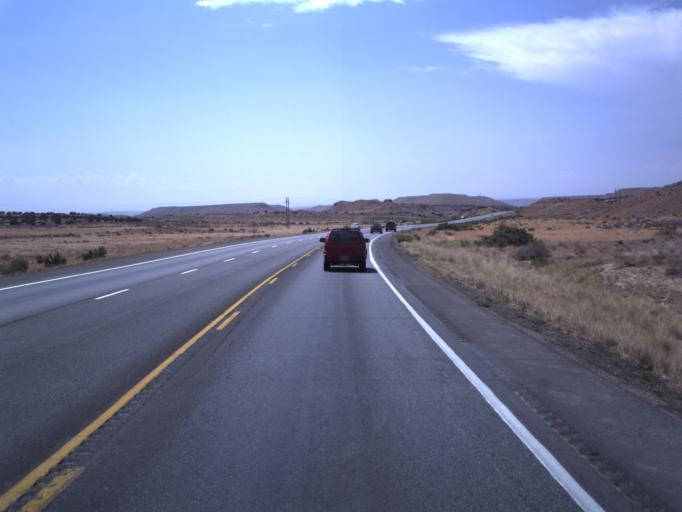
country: US
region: Utah
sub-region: Uintah County
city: Maeser
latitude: 40.3957
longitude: -109.5928
